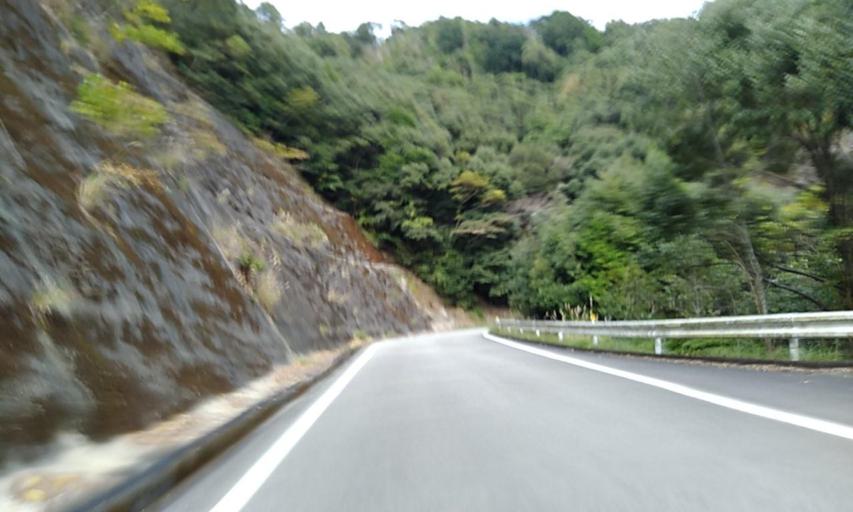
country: JP
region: Wakayama
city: Shingu
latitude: 33.5429
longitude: 135.8322
